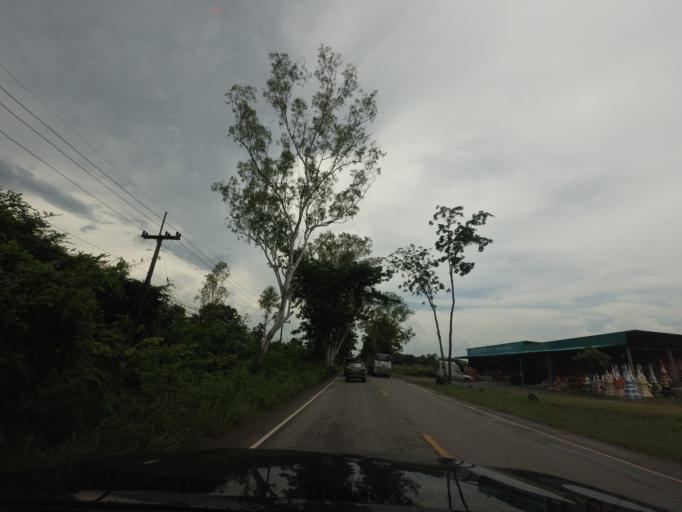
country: TH
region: Khon Kaen
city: Nong Na Kham
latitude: 16.7960
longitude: 102.3434
